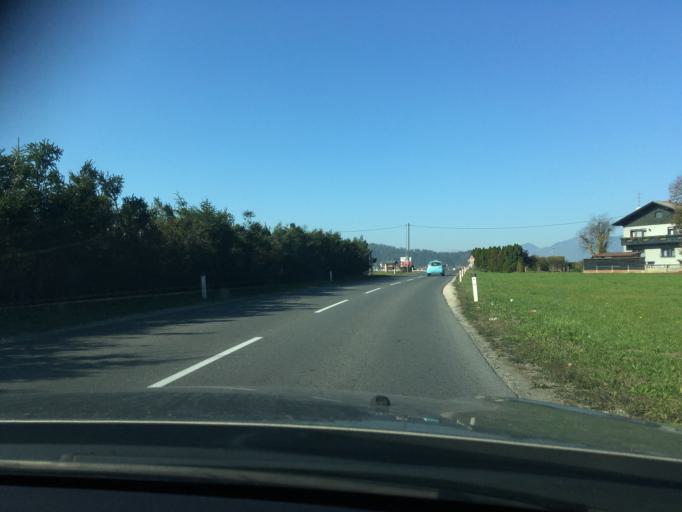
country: SI
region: Domzale
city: Domzale
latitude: 46.1513
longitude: 14.5911
